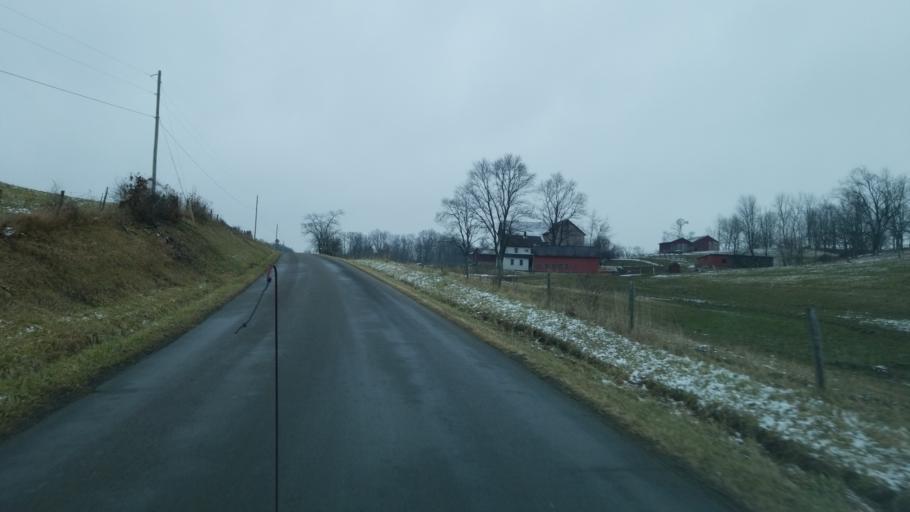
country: US
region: Ohio
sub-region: Wayne County
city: Apple Creek
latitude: 40.6986
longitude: -81.8618
